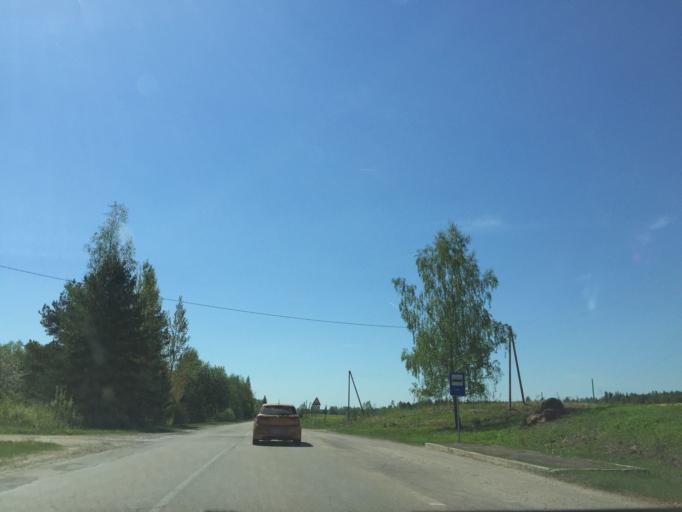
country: LV
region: Malpils
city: Malpils
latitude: 56.9257
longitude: 24.9375
